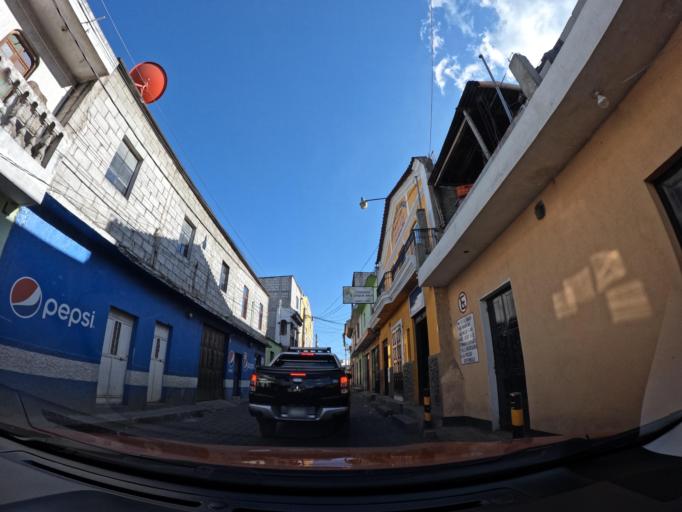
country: GT
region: Sacatepequez
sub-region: Municipio de Santa Maria de Jesus
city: Santa Maria de Jesus
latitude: 14.4934
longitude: -90.7086
